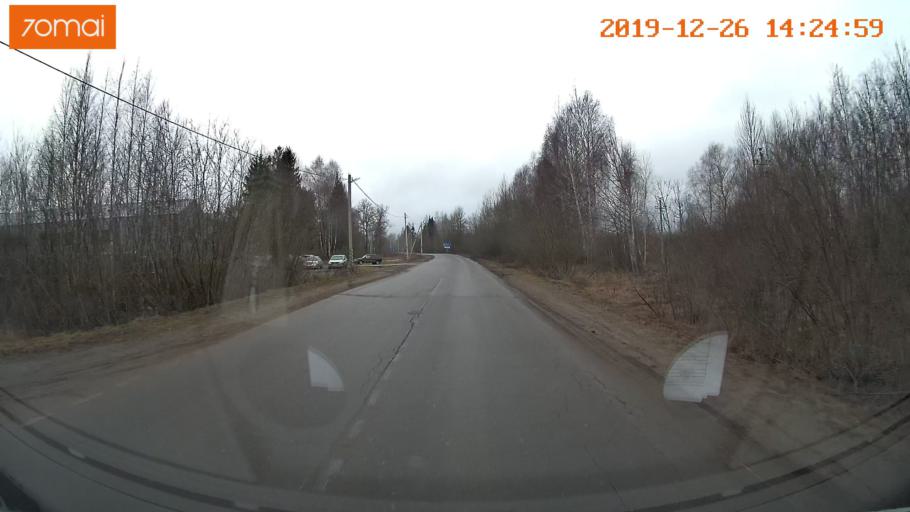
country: RU
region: Jaroslavl
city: Poshekhon'ye
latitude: 58.4965
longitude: 39.0989
